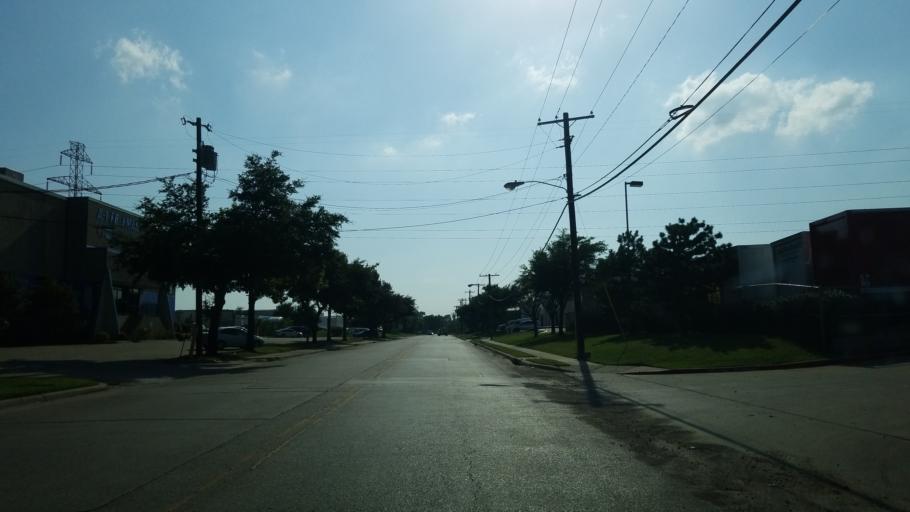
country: US
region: Texas
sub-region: Dallas County
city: Farmers Branch
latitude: 32.8739
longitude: -96.9035
